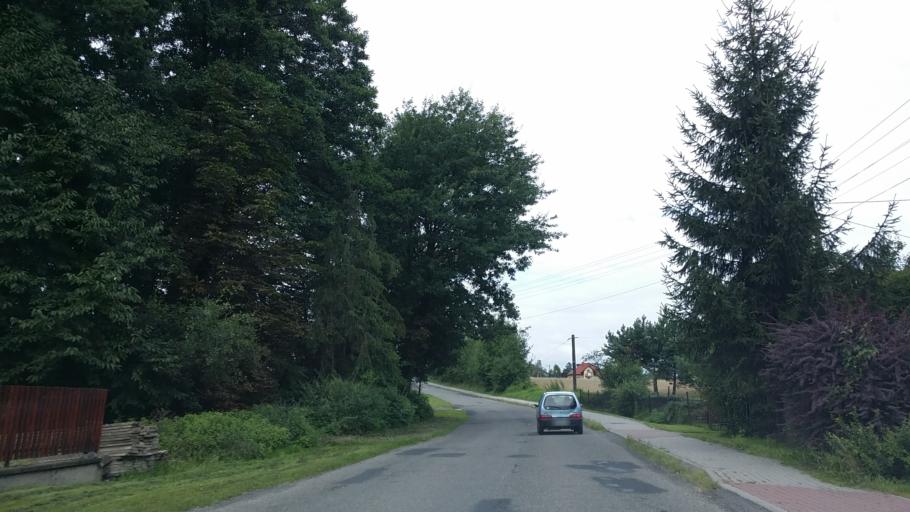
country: PL
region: Lesser Poland Voivodeship
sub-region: Powiat wadowicki
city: Tomice
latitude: 49.8985
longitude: 19.4712
